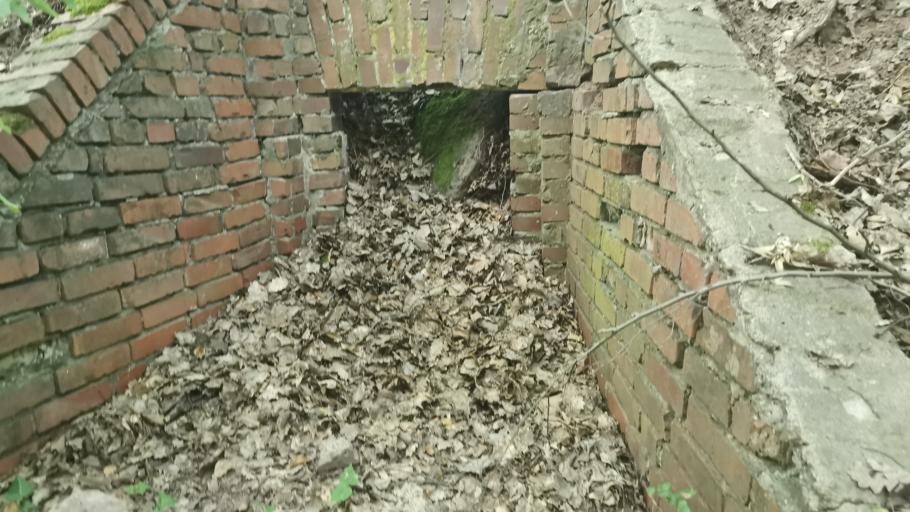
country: DE
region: Bavaria
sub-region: Regierungsbezirk Mittelfranken
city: Schwaig
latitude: 49.4491
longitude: 11.1492
